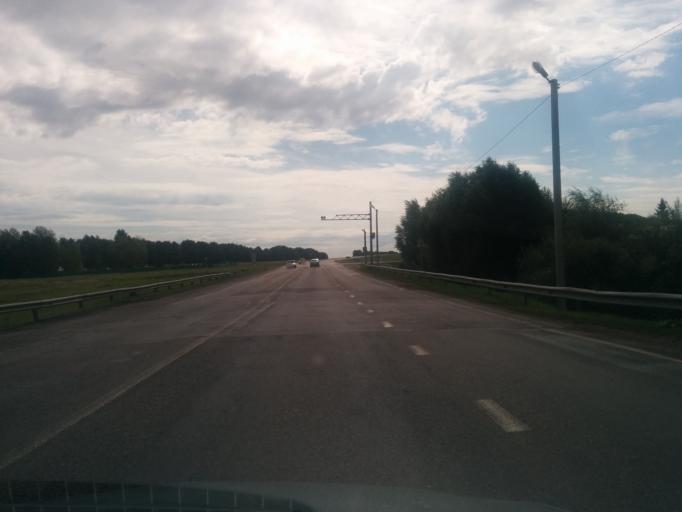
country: RU
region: Bashkortostan
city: Kabakovo
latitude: 54.4657
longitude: 55.9570
